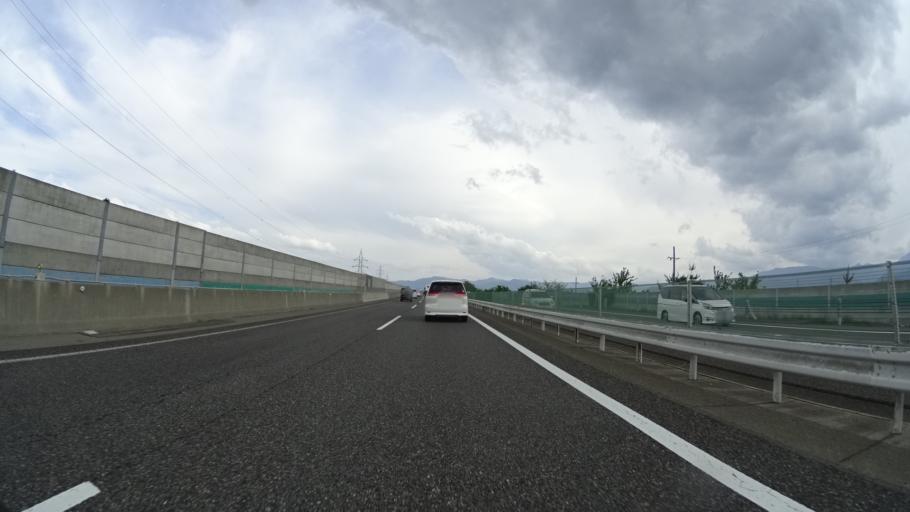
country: JP
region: Nagano
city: Matsumoto
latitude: 36.1890
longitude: 137.9373
